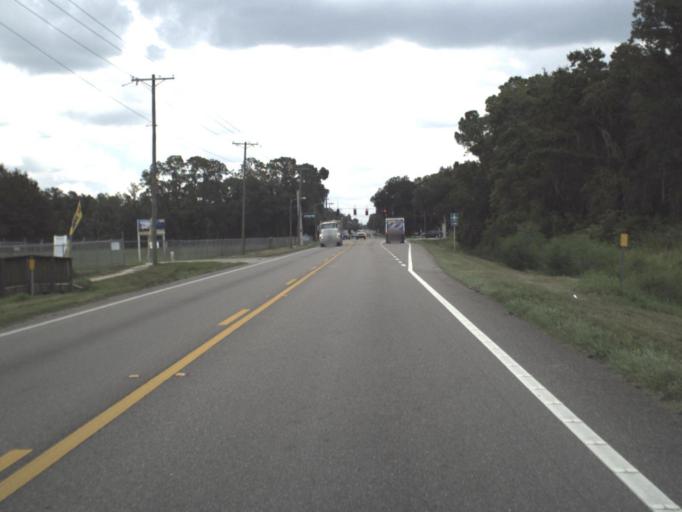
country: US
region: Florida
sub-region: Hillsborough County
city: Dover
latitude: 28.0205
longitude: -82.1774
